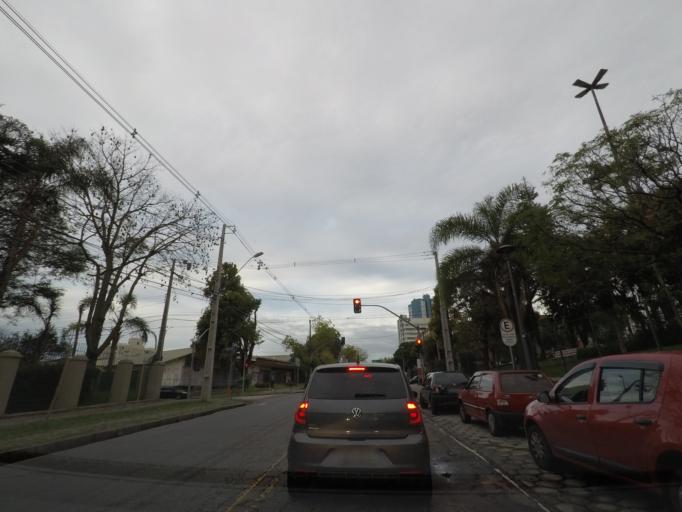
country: BR
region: Parana
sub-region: Curitiba
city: Curitiba
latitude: -25.4354
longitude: -49.2460
